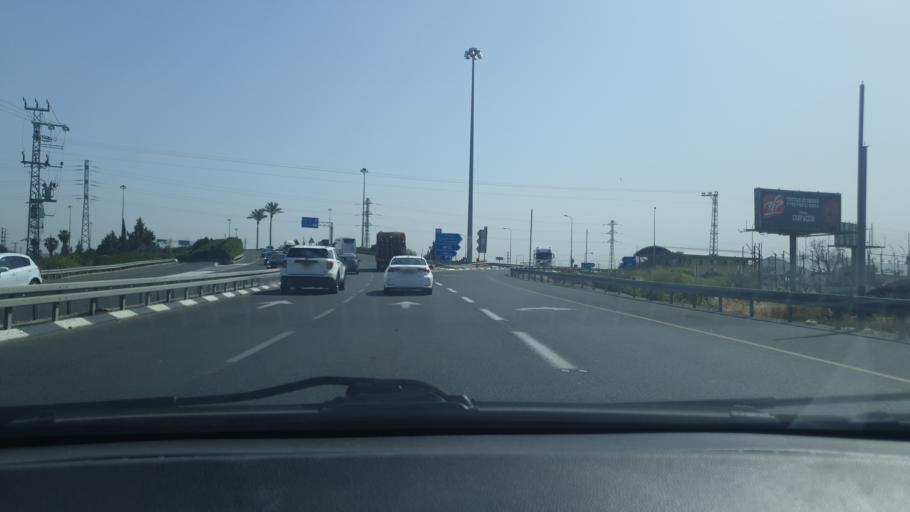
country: IL
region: Central District
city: Bet Dagan
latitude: 32.0058
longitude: 34.8332
